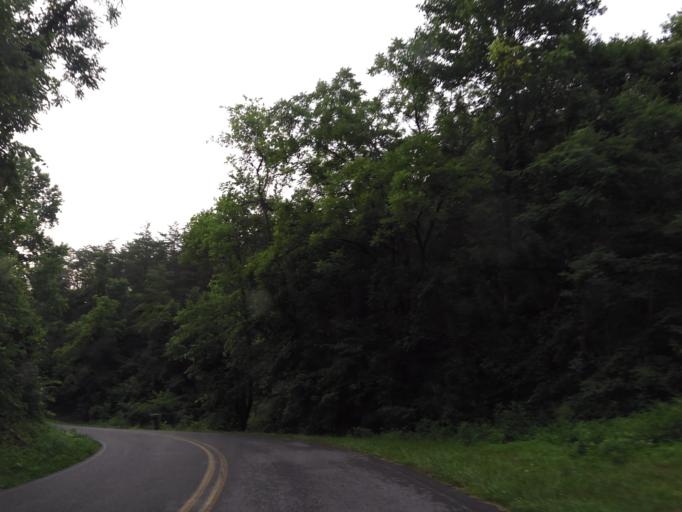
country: US
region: Tennessee
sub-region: Sevier County
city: Seymour
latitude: 35.8390
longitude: -83.6862
